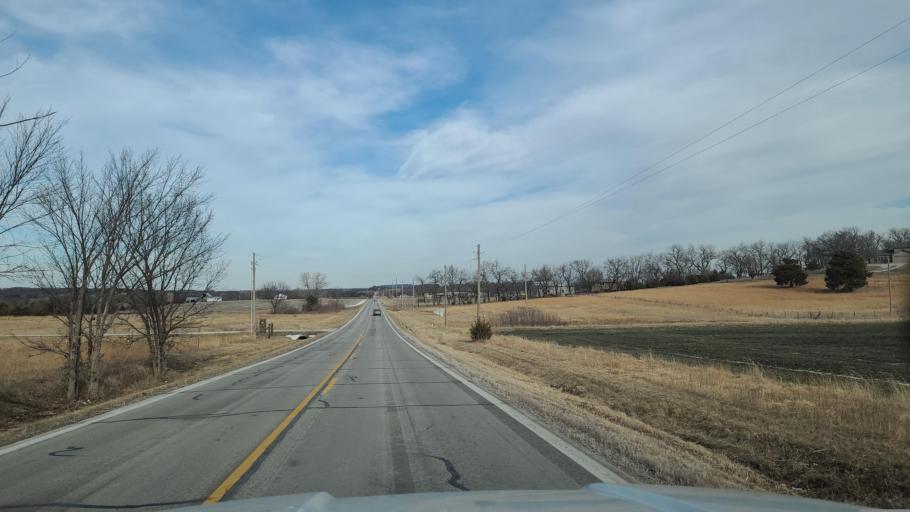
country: US
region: Kansas
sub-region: Douglas County
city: Baldwin City
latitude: 38.8308
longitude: -95.1864
